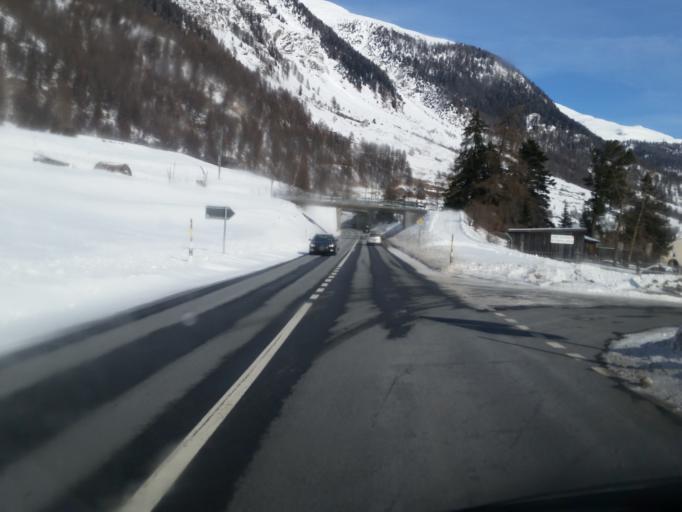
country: CH
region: Grisons
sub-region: Inn District
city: Zernez
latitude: 46.7648
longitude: 10.1066
